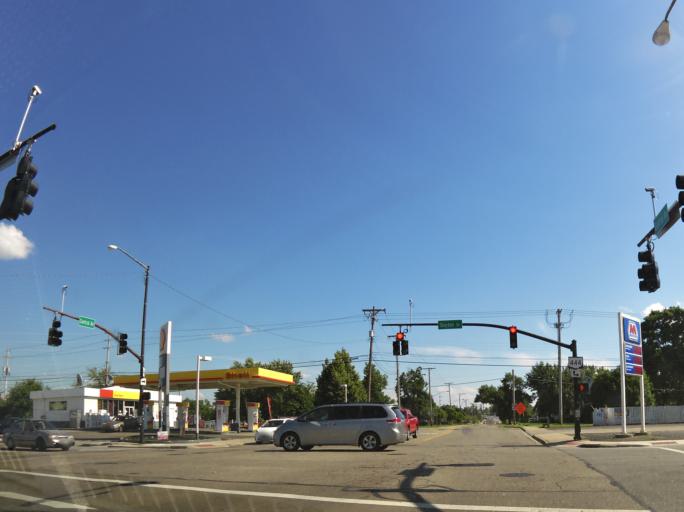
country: US
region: Ohio
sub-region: Greene County
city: Fairborn
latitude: 39.8194
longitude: -84.0214
